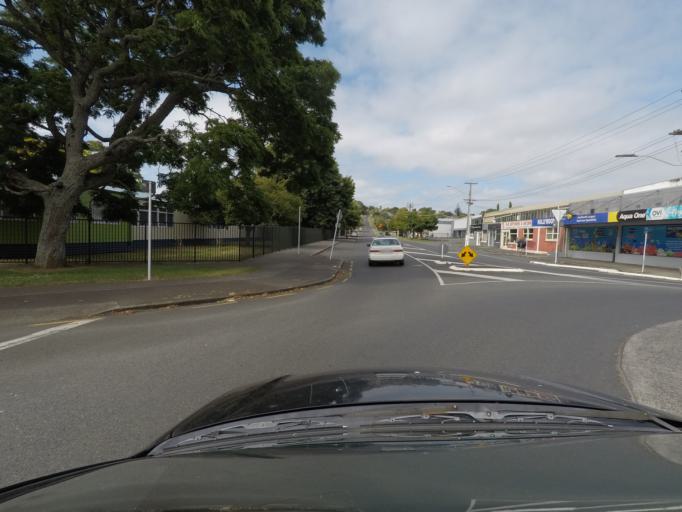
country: NZ
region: Auckland
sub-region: Auckland
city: Auckland
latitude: -36.9118
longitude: 174.7485
